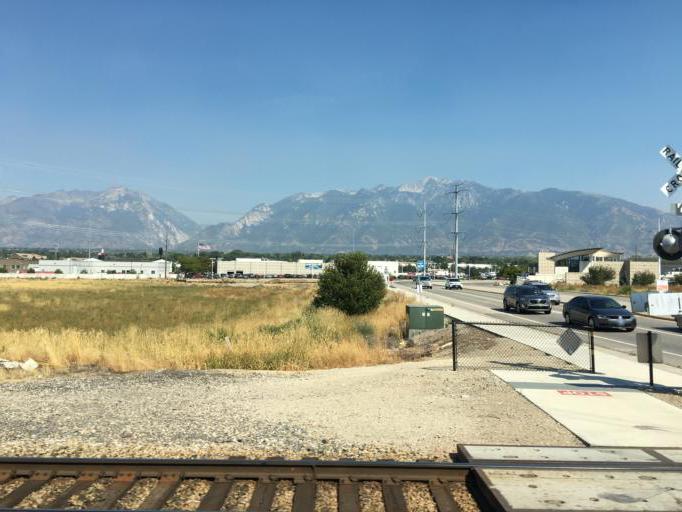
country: US
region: Utah
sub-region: Salt Lake County
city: South Jordan
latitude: 40.5544
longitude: -111.9017
